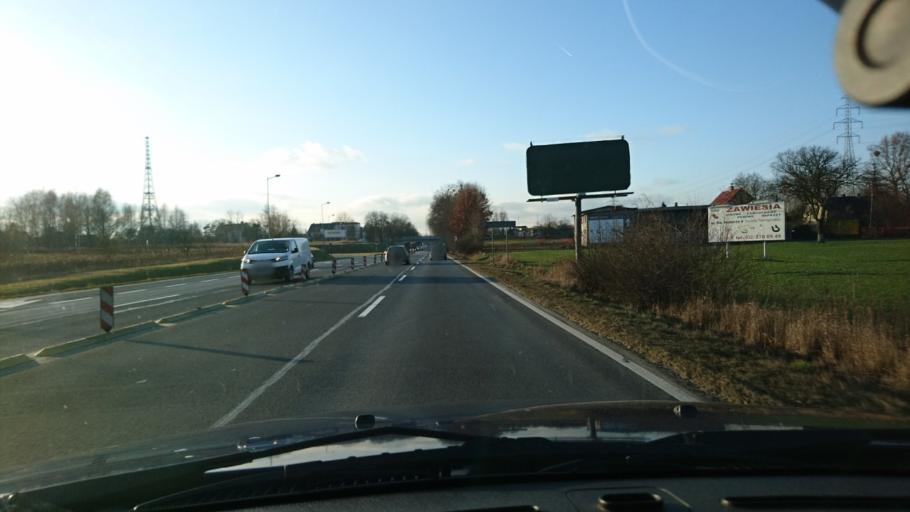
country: PL
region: Silesian Voivodeship
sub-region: Gliwice
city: Gliwice
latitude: 50.3144
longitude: 18.6977
